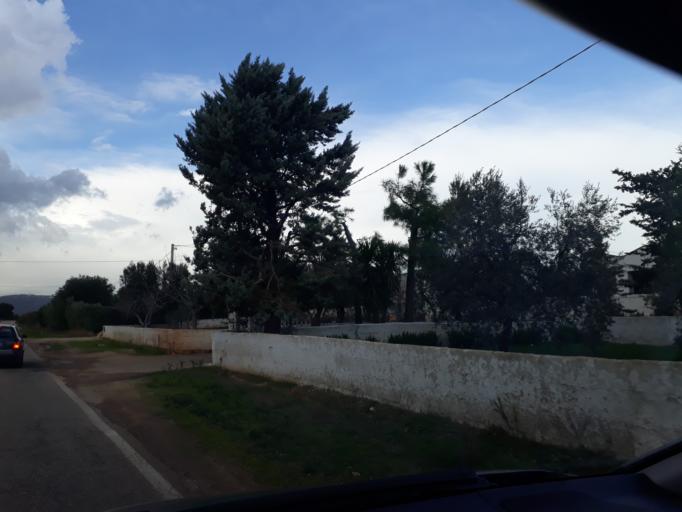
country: IT
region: Apulia
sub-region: Provincia di Brindisi
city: Pezze di Greco
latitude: 40.8016
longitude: 17.4000
